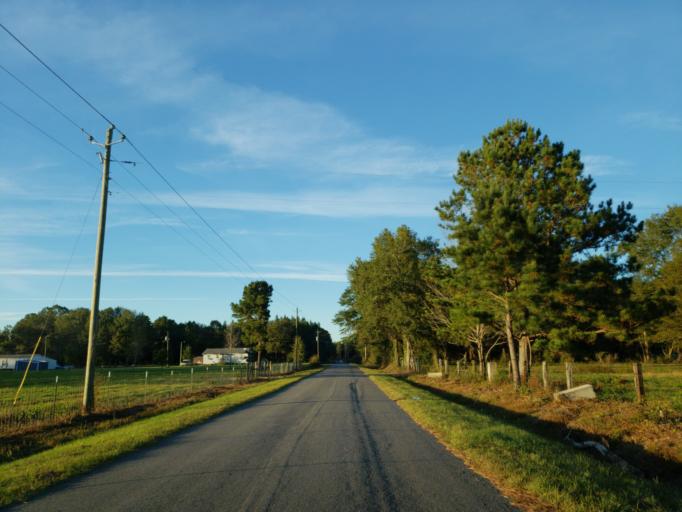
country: US
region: Mississippi
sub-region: Wayne County
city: Belmont
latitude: 31.4626
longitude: -88.5207
